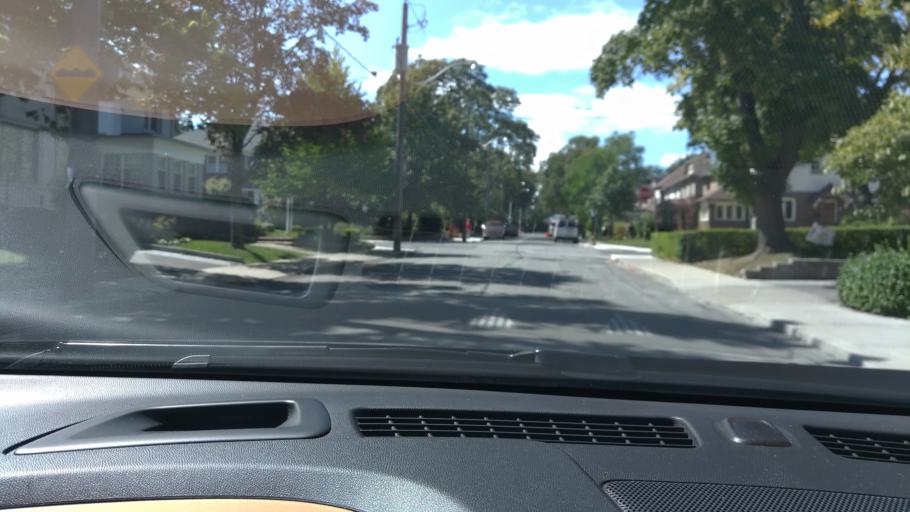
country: CA
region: Ontario
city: Toronto
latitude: 43.7027
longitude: -79.4007
